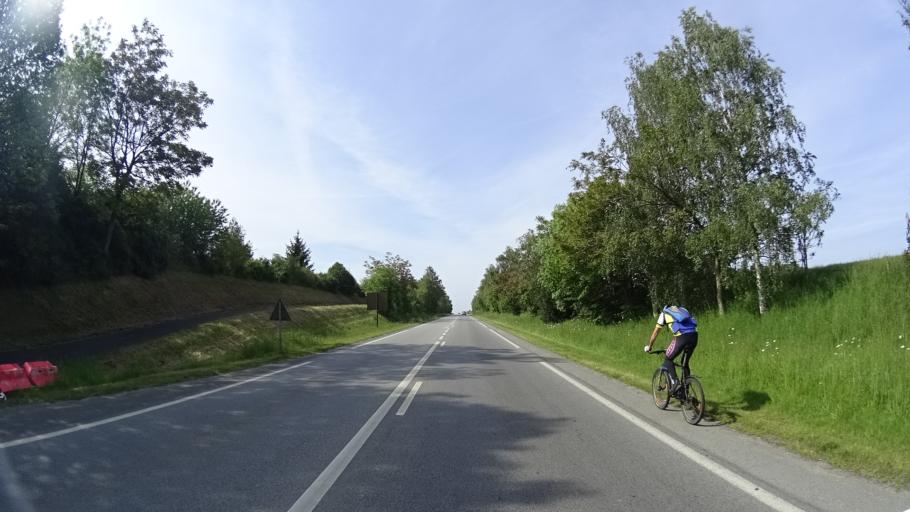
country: FR
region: Brittany
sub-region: Departement d'Ille-et-Vilaine
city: Chateaugiron
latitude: 48.0524
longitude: -1.5124
